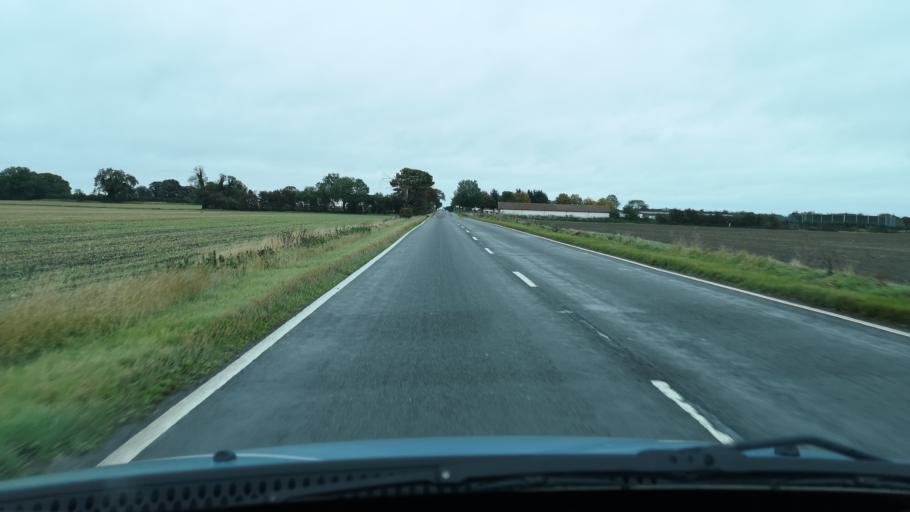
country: GB
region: England
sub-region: Doncaster
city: Hatfield
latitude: 53.5892
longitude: -0.9256
